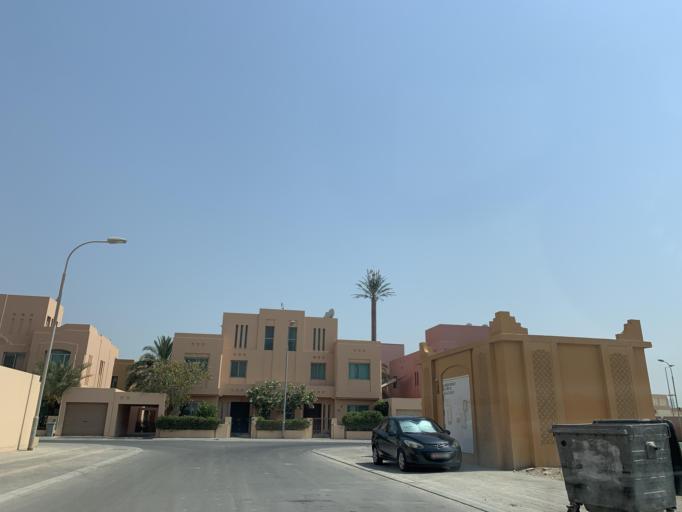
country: BH
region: Manama
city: Jidd Hafs
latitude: 26.2085
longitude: 50.5245
